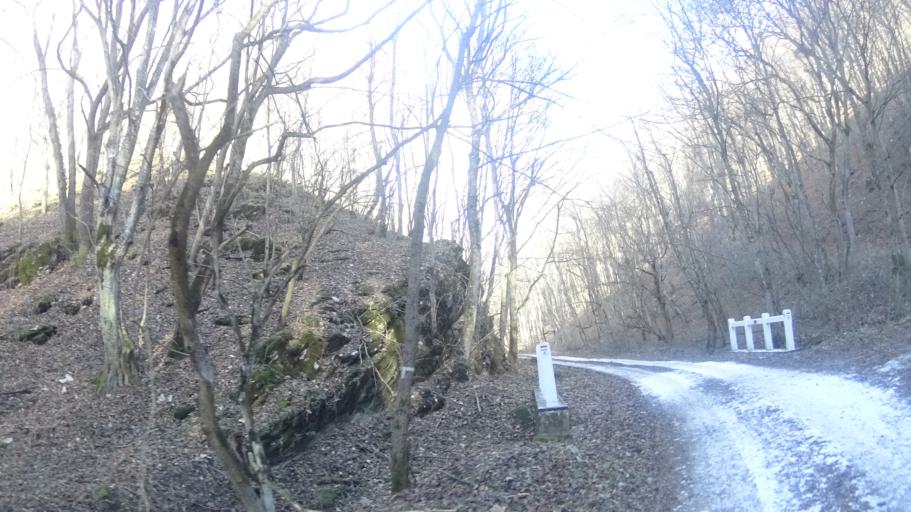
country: HU
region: Borsod-Abauj-Zemplen
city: Bogacs
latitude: 47.9993
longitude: 20.5205
